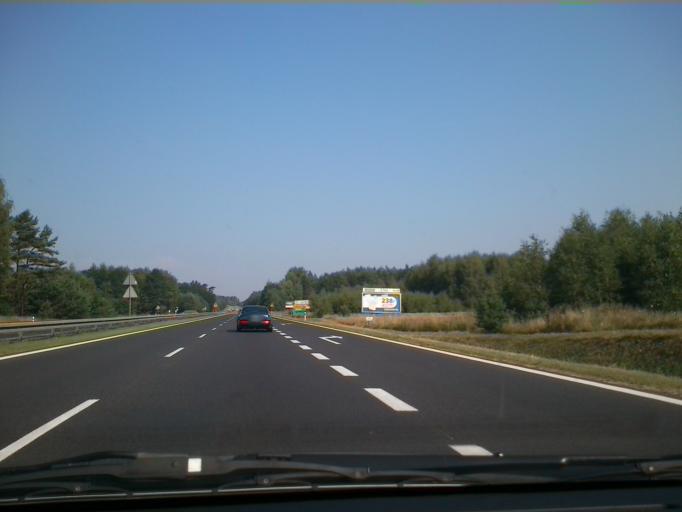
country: PL
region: Lubusz
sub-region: Zielona Gora
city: Zielona Gora
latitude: 51.9230
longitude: 15.5647
